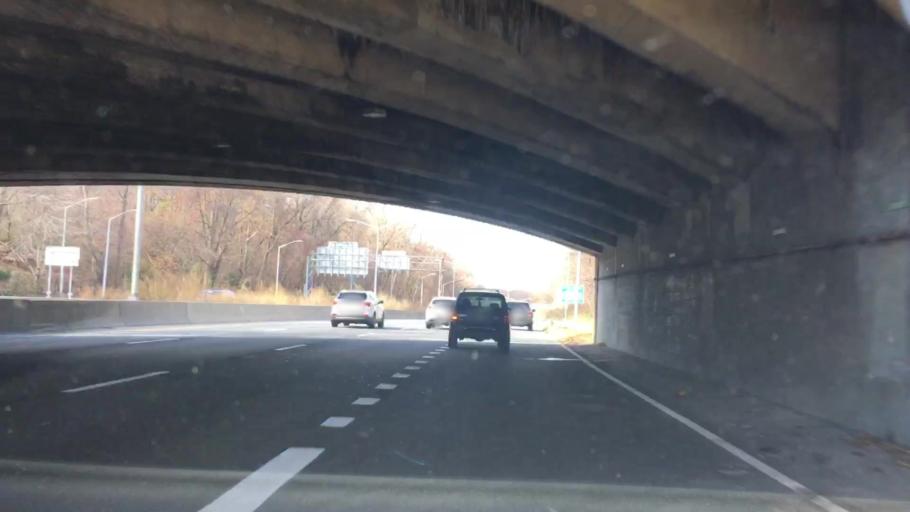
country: US
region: New York
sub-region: Nassau County
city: Bellerose Terrace
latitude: 40.7457
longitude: -73.7350
